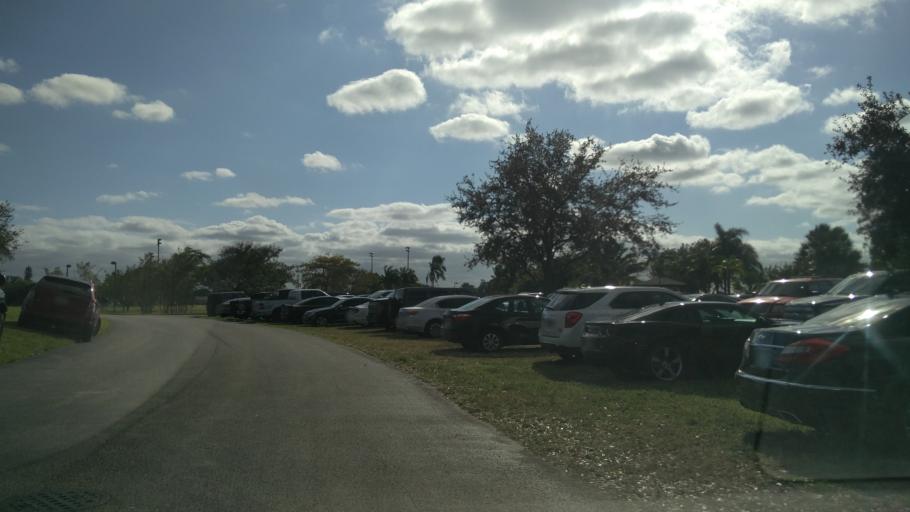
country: US
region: Florida
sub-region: Broward County
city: Rock Island
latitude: 26.1581
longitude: -80.1626
